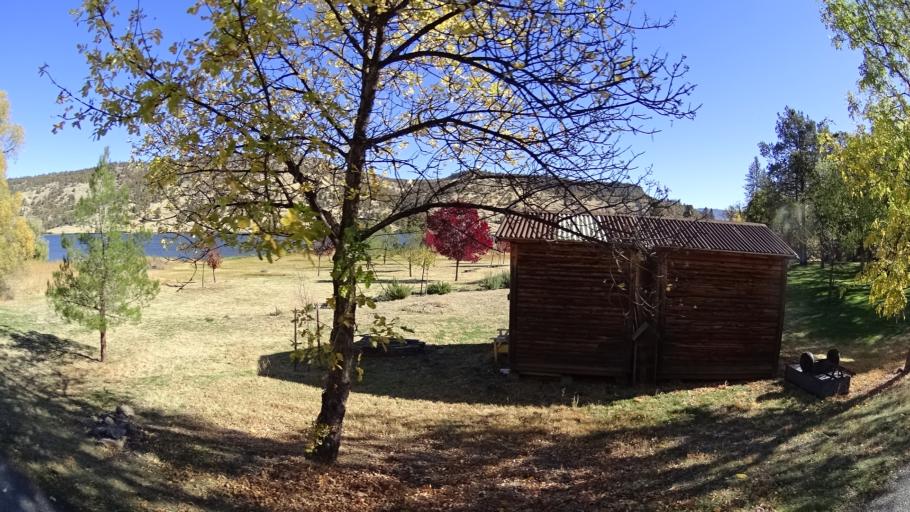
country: US
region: California
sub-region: Siskiyou County
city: Montague
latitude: 41.9679
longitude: -122.2859
